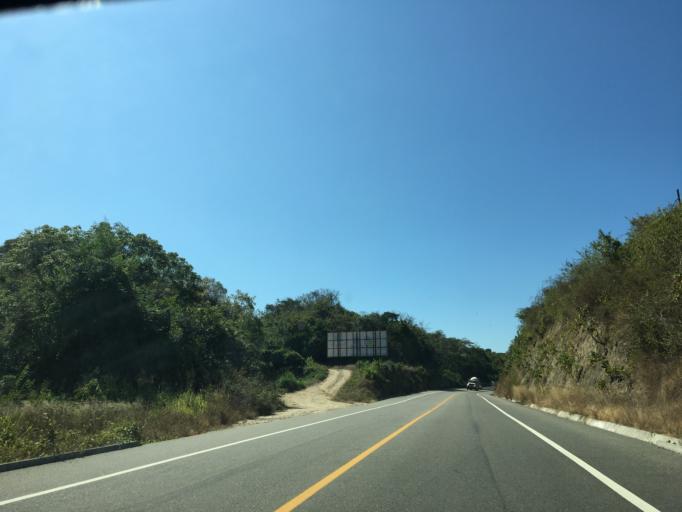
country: MX
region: Oaxaca
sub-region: Santa Maria Huatulco
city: Cuapinolito (Azulillo)
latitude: 15.7727
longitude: -96.2437
